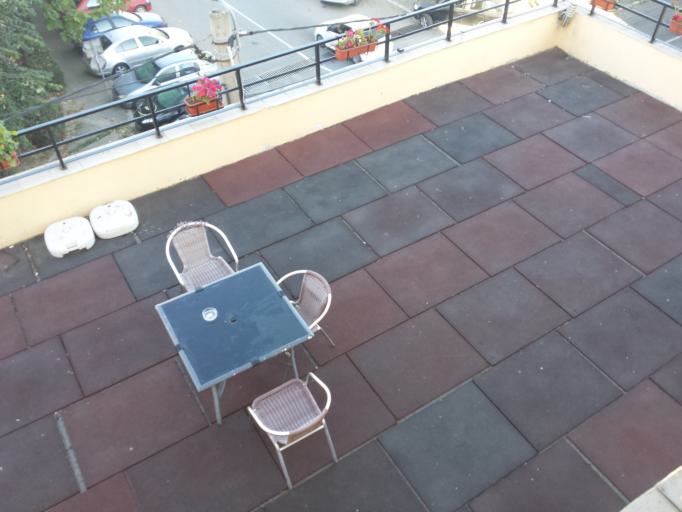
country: RO
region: Tulcea
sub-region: Municipiul Tulcea
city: Tulcea
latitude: 45.1731
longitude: 28.7881
